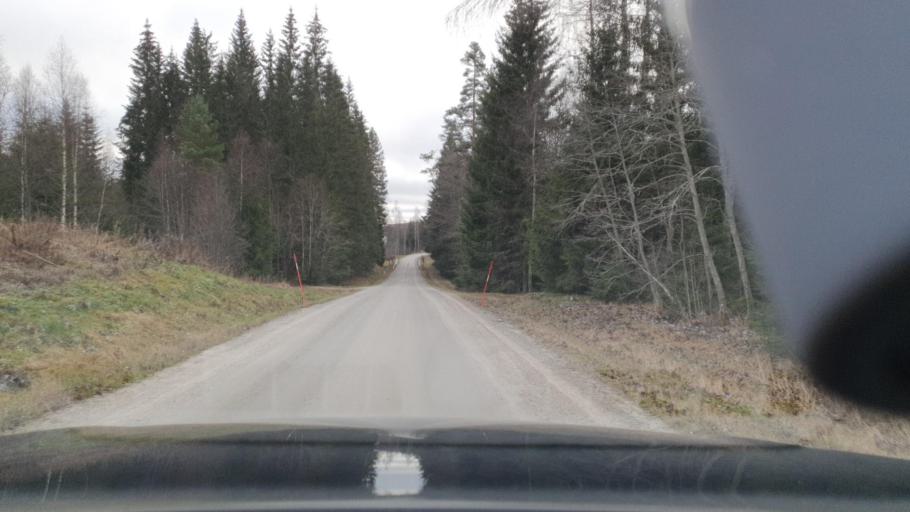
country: SE
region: Vaermland
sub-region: Arvika Kommun
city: Arvika
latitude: 59.8194
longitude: 12.7440
